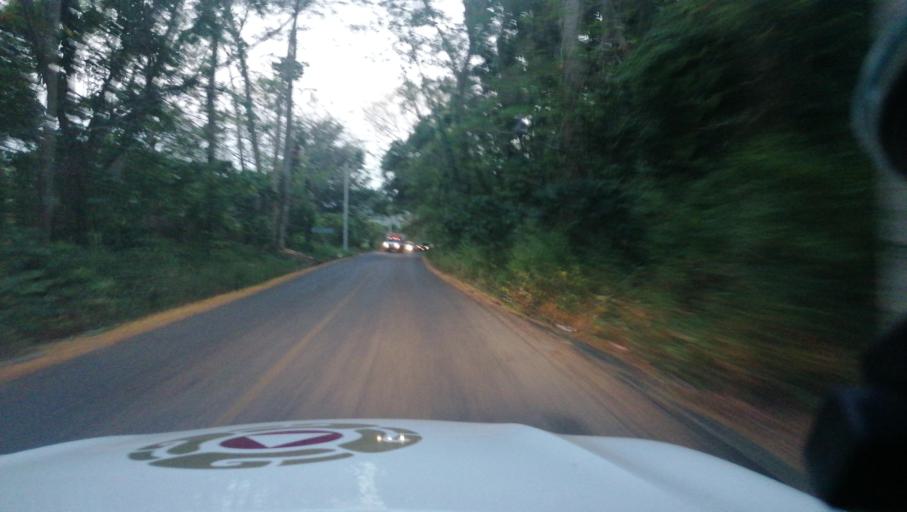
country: MX
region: Chiapas
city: Veinte de Noviembre
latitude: 15.0129
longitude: -92.2462
